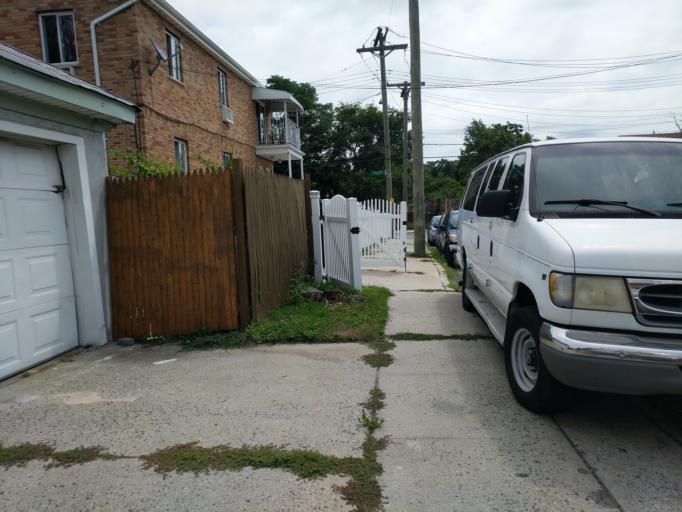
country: US
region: New York
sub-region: Nassau County
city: South Valley Stream
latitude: 40.6557
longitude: -73.7269
